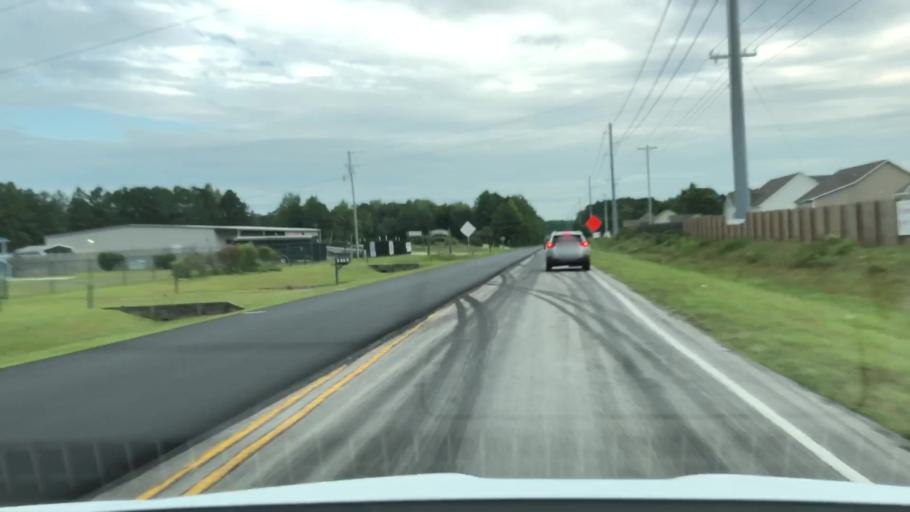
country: US
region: North Carolina
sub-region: Carteret County
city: Cape Carteret
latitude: 34.7595
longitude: -77.0946
